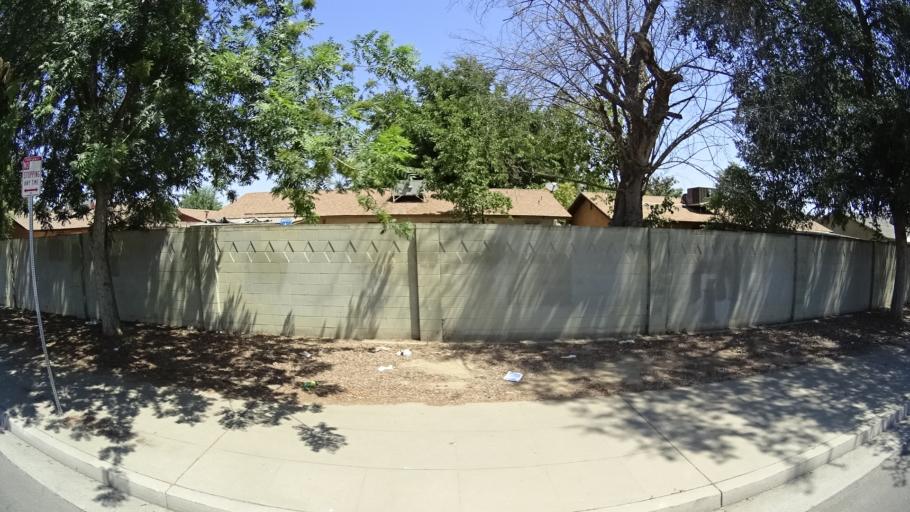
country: US
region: California
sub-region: Fresno County
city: Fresno
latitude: 36.7141
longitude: -119.7979
